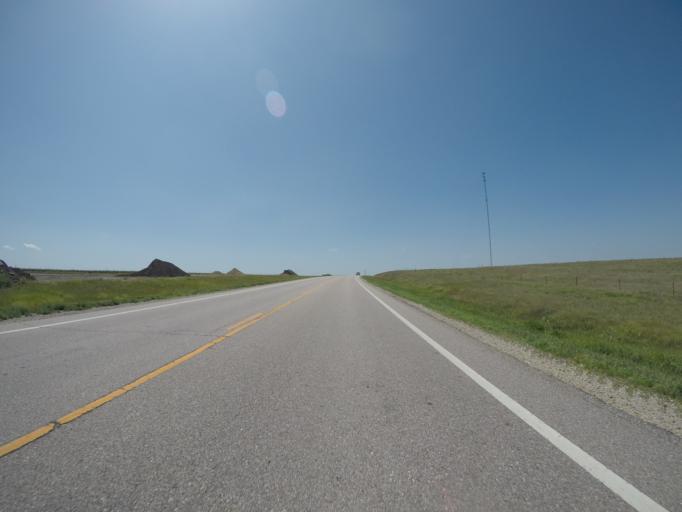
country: US
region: Kansas
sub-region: Osborne County
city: Osborne
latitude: 39.4801
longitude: -98.6946
